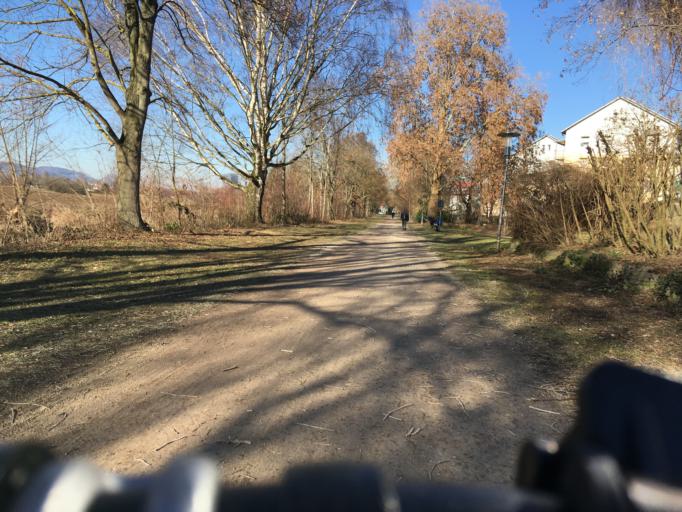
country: DE
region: Baden-Wuerttemberg
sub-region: Freiburg Region
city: Rielasingen-Worblingen
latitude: 47.7441
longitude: 8.8412
